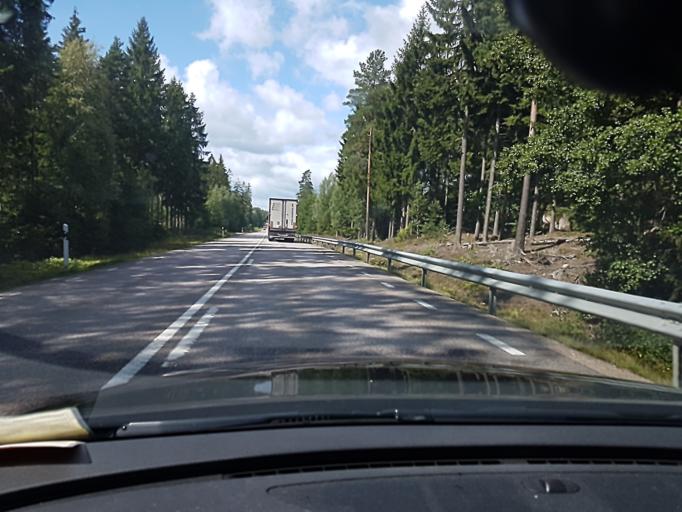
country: SE
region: Kronoberg
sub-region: Lessebo Kommun
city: Hovmantorp
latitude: 56.7868
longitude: 15.1784
